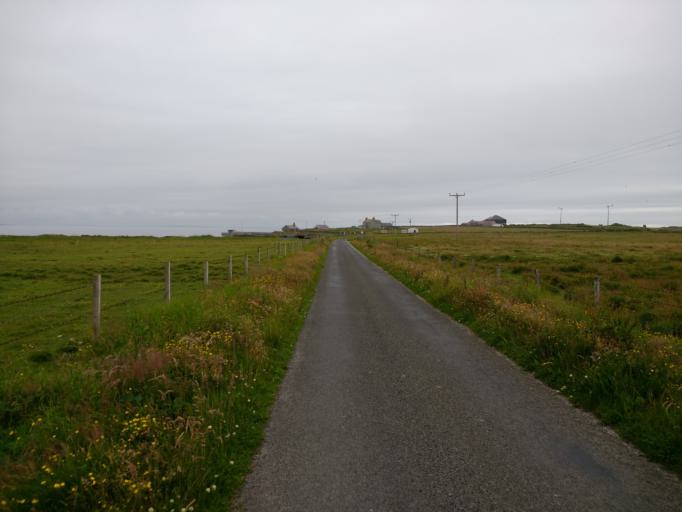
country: GB
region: Scotland
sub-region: Orkney Islands
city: Kirkwall
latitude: 59.3602
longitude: -2.4367
